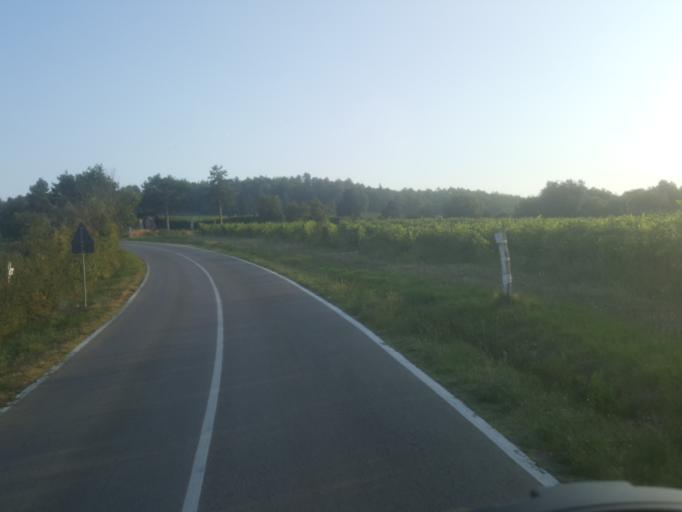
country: IT
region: Tuscany
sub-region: Province of Florence
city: Montaione
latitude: 43.5367
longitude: 10.9241
